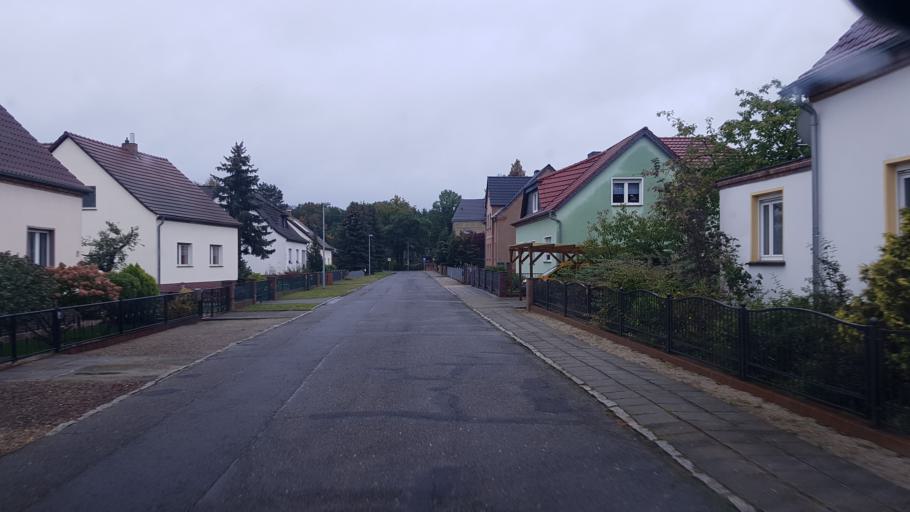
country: DE
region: Brandenburg
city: Altdobern
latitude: 51.6502
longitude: 14.0155
